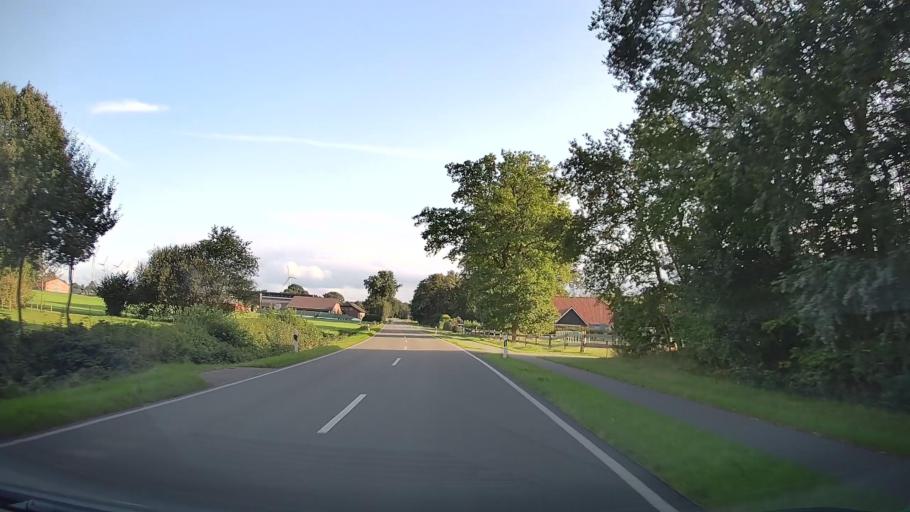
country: DE
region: Lower Saxony
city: Barssel
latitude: 53.0902
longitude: 7.7133
